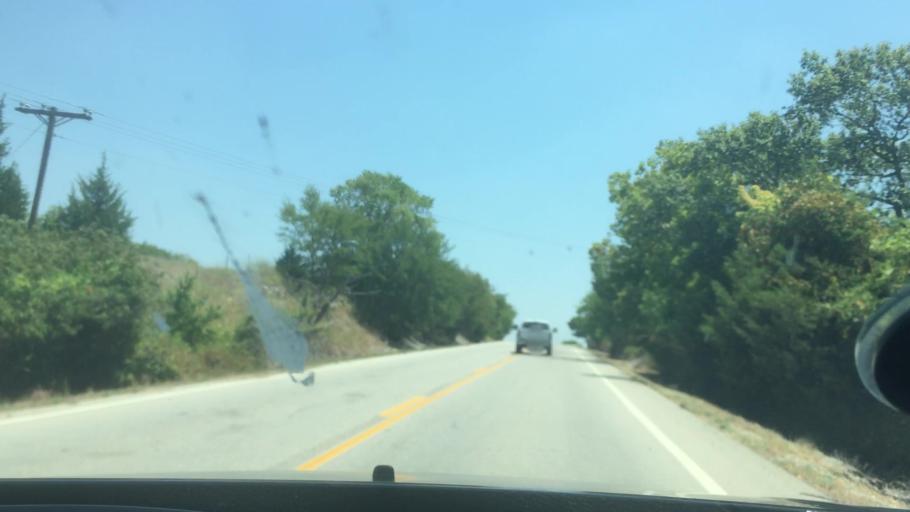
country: US
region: Oklahoma
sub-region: Bryan County
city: Durant
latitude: 34.1674
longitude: -96.4039
